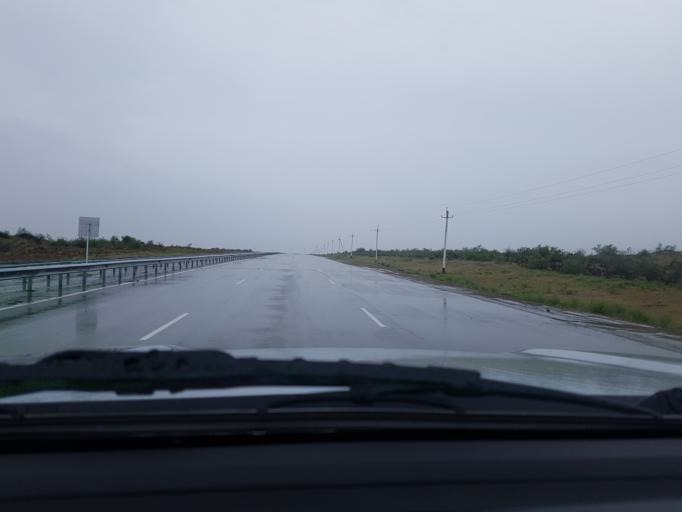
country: TM
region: Lebap
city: Farap
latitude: 39.2079
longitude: 63.6849
